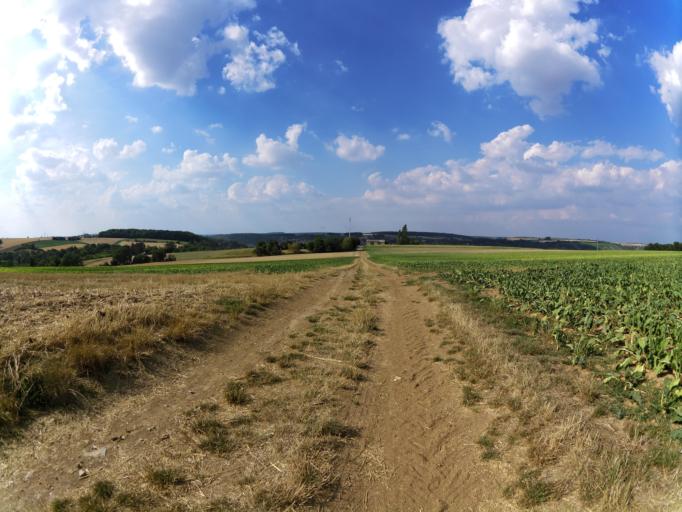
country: DE
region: Bavaria
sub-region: Regierungsbezirk Unterfranken
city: Ochsenfurt
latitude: 49.6525
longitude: 10.0641
